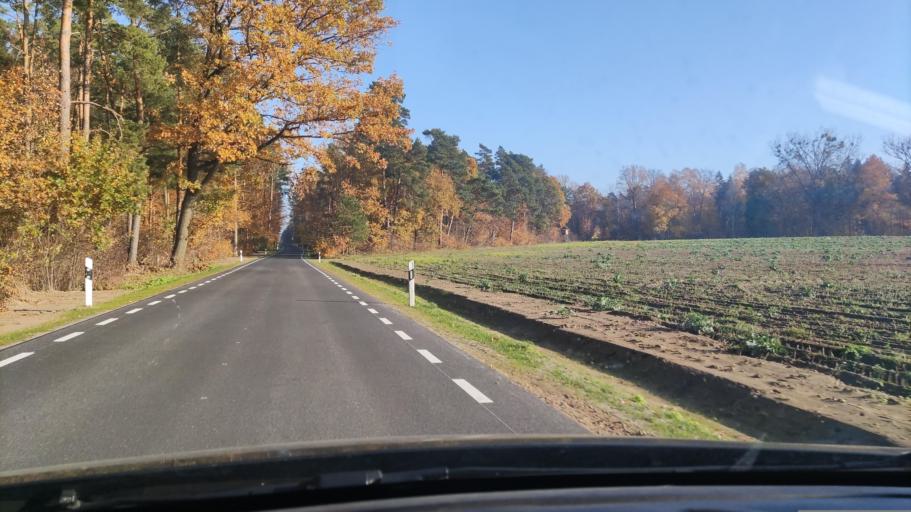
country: DE
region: Brandenburg
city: Furstenberg
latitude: 53.2292
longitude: 13.0553
